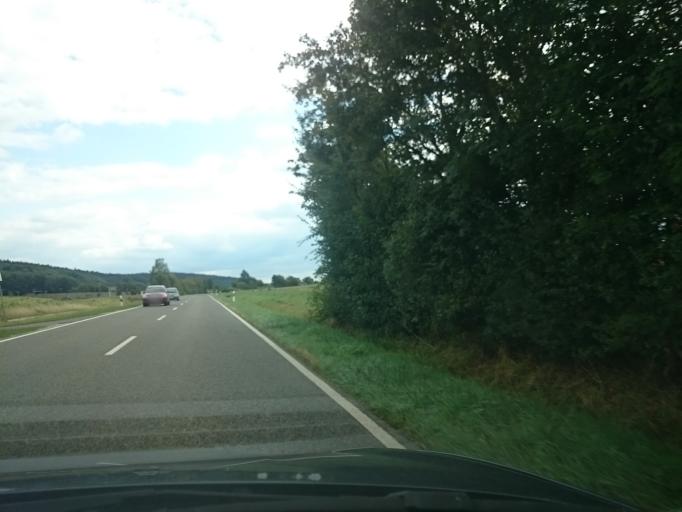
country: DE
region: Bavaria
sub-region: Regierungsbezirk Mittelfranken
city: Thalmassing
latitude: 49.1335
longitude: 11.2675
